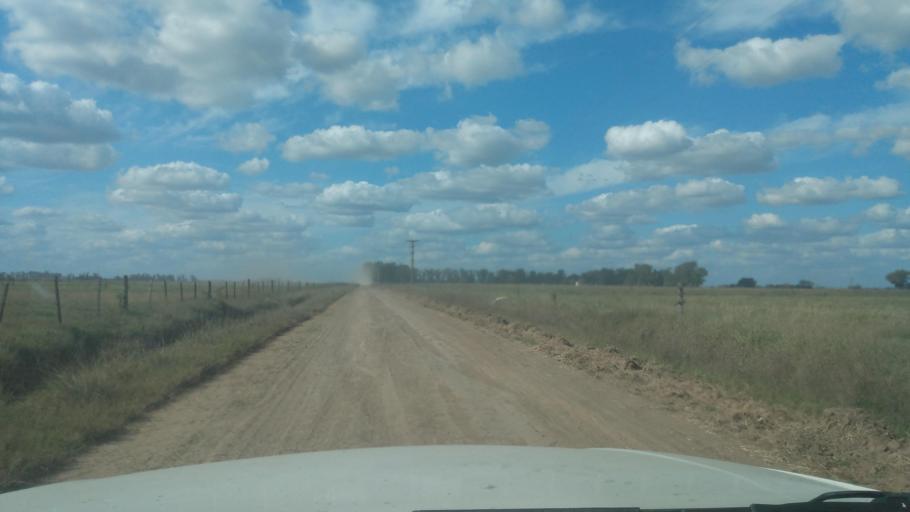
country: AR
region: Buenos Aires
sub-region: Partido de Navarro
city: Navarro
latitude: -35.0358
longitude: -59.5070
